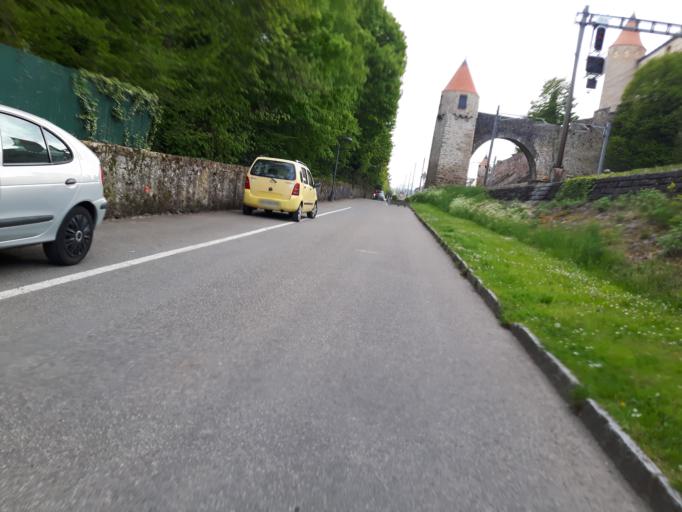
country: CH
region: Vaud
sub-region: Jura-Nord vaudois District
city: Grandson
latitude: 46.8099
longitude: 6.6486
